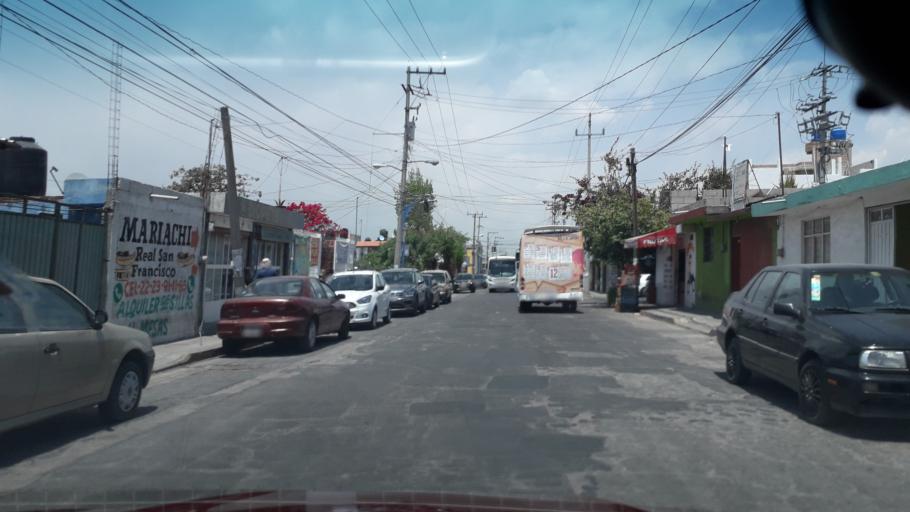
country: MX
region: Puebla
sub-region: Puebla
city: El Capulo (La Quebradora)
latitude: 18.9901
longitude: -98.2475
